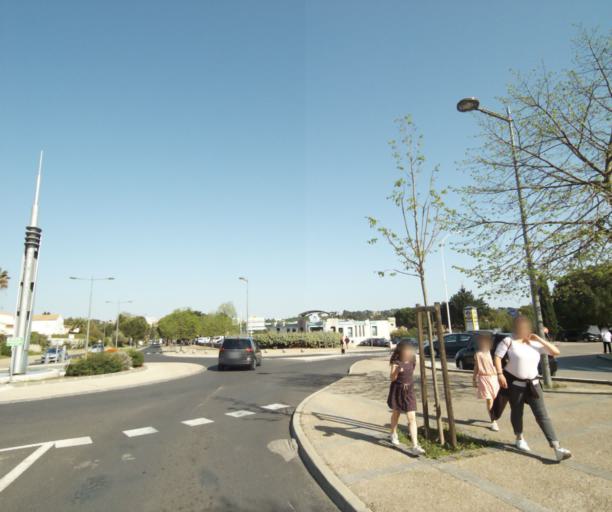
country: FR
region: Languedoc-Roussillon
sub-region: Departement de l'Herault
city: Juvignac
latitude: 43.6139
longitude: 3.8105
